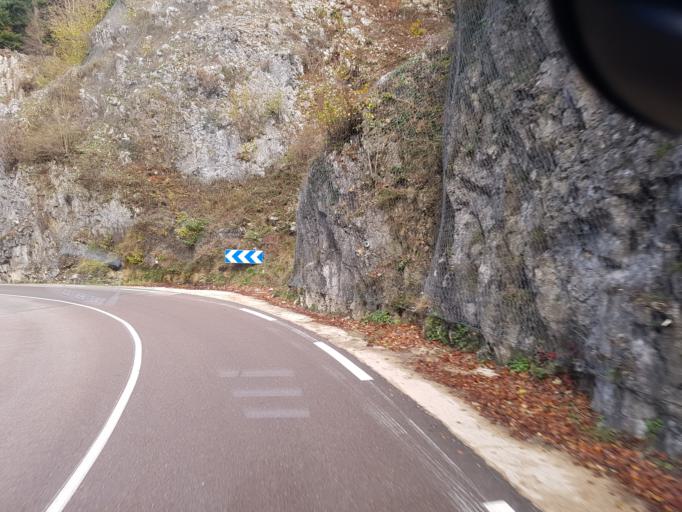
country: FR
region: Franche-Comte
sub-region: Departement du Jura
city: Champagnole
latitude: 46.6668
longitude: 5.9459
